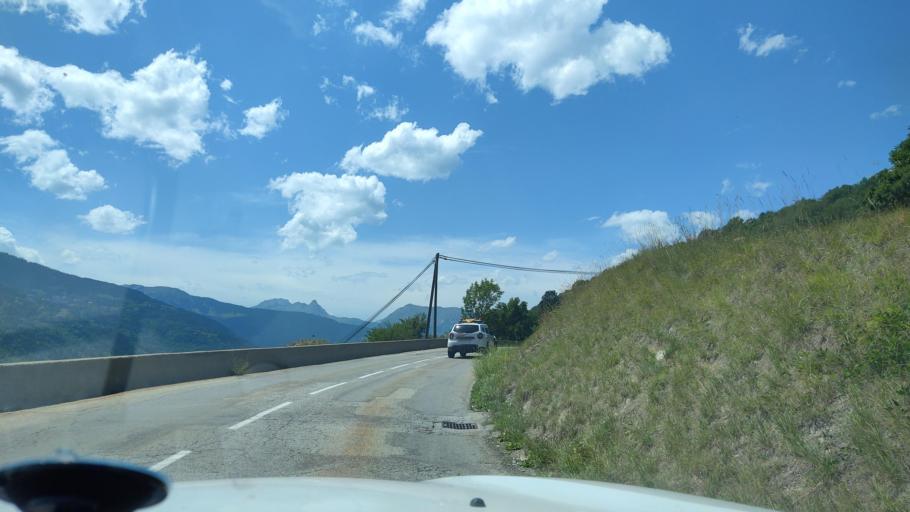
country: FR
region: Rhone-Alpes
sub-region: Departement de la Savoie
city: Bozel
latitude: 45.4472
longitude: 6.6420
